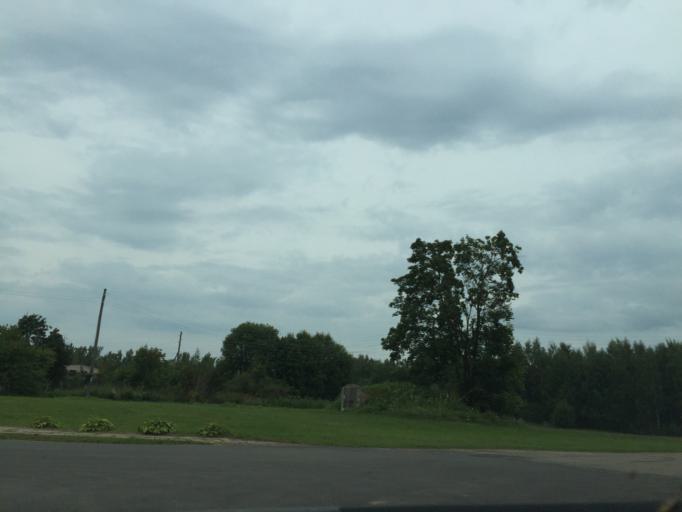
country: LV
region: Zilupes
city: Zilupe
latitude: 56.3905
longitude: 28.1369
